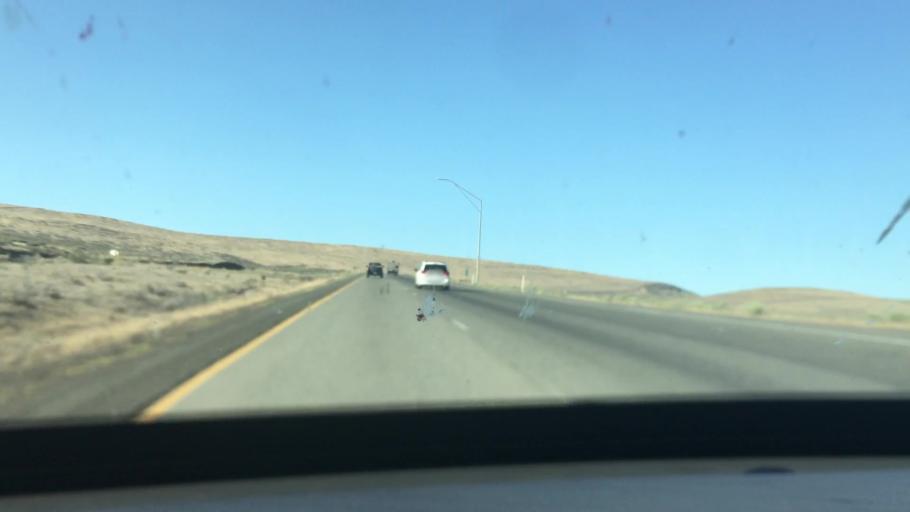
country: US
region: Washington
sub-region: Yakima County
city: Terrace Heights
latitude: 46.7155
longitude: -120.4108
